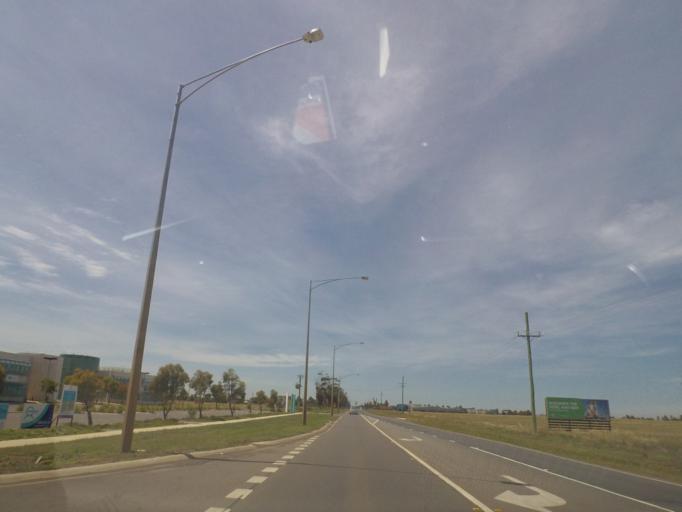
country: AU
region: Victoria
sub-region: Wyndham
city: Tarneit
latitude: -37.8714
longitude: 144.6119
